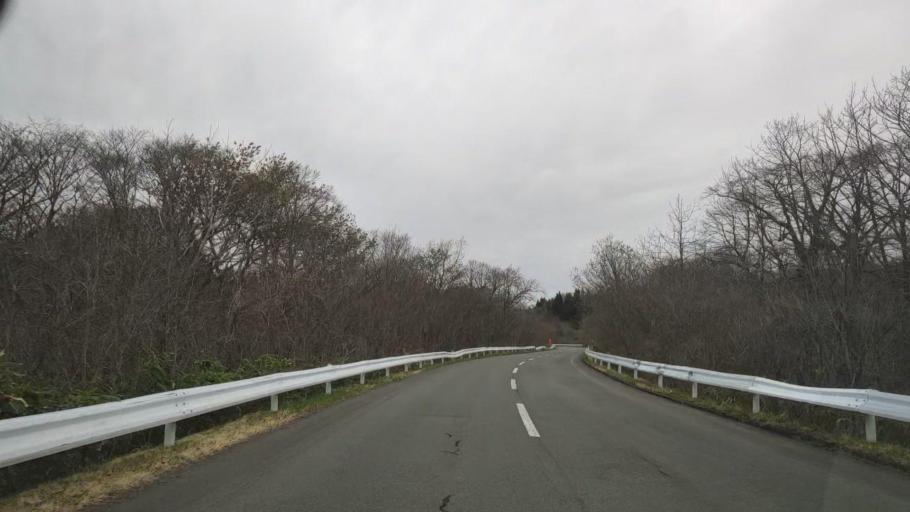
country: JP
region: Akita
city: Hanawa
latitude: 40.4090
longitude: 140.8493
